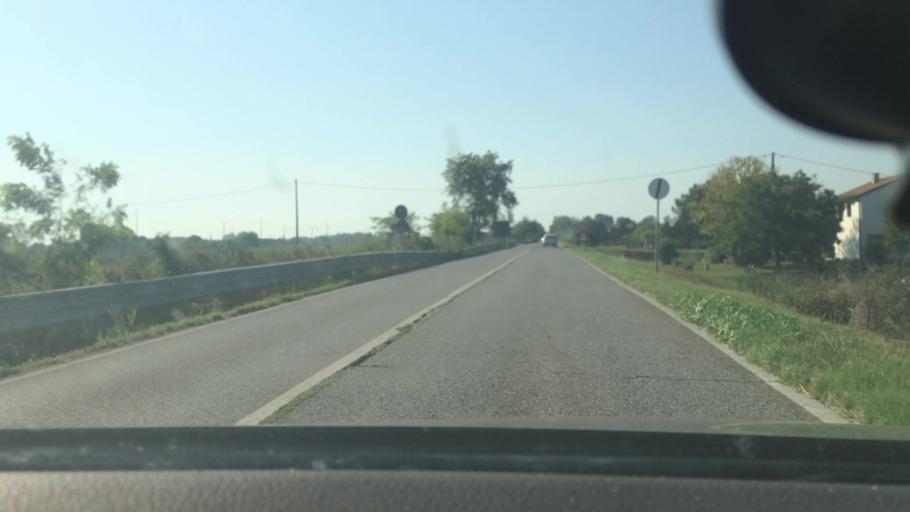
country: IT
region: Emilia-Romagna
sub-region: Provincia di Ferrara
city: Comacchio
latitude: 44.7124
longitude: 12.1600
